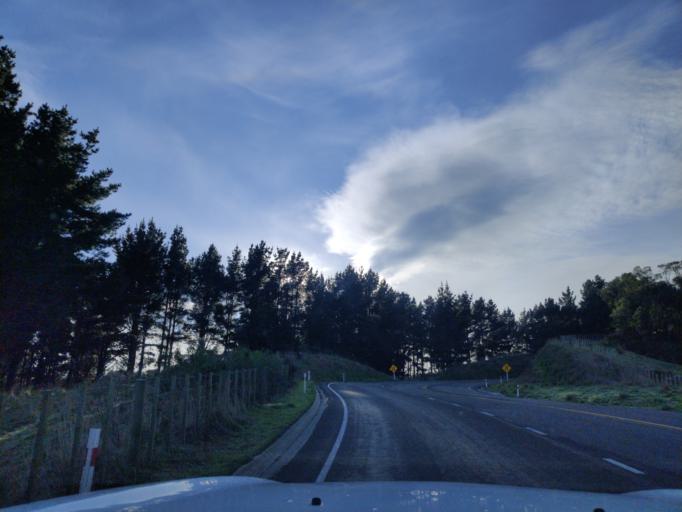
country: NZ
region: Manawatu-Wanganui
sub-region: Palmerston North City
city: Palmerston North
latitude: -40.2858
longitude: 175.7890
